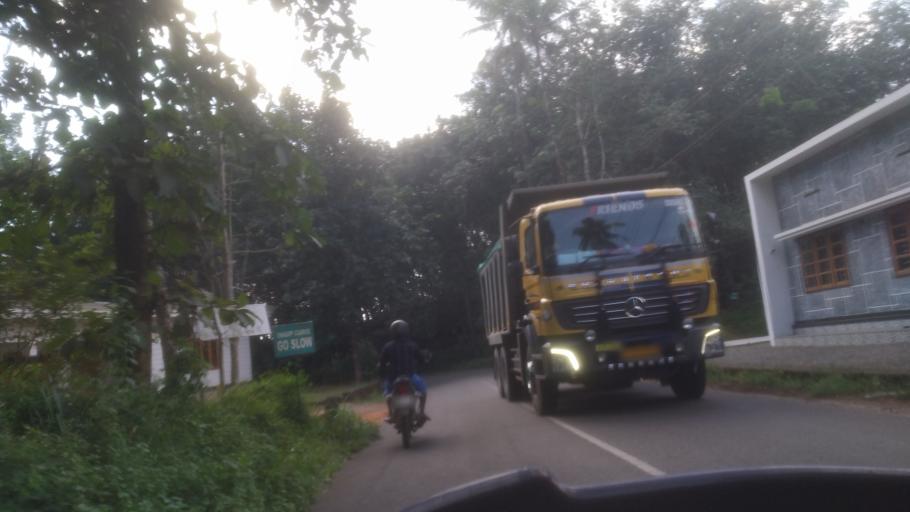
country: IN
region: Kerala
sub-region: Ernakulam
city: Kotamangalam
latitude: 10.0060
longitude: 76.6710
